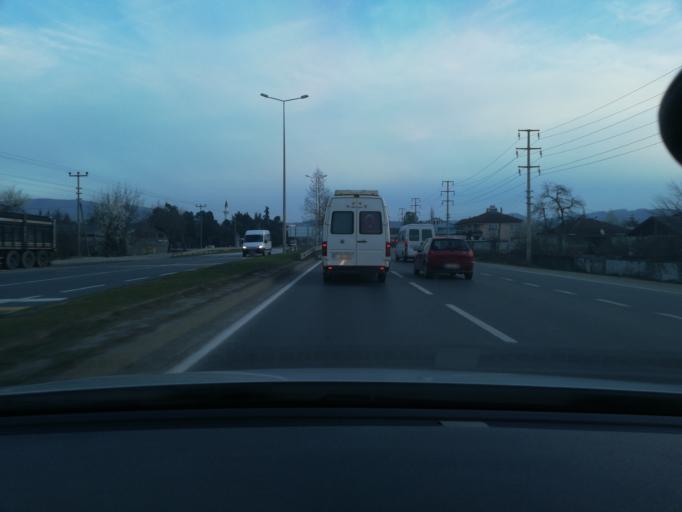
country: TR
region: Duzce
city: Konuralp
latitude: 40.8775
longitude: 31.1700
